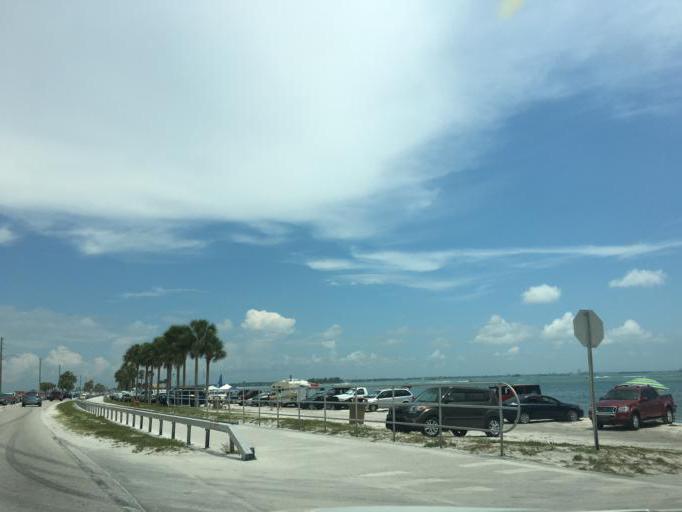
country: US
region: Florida
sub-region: Pinellas County
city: Palm Harbor
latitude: 28.0586
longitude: -82.8098
